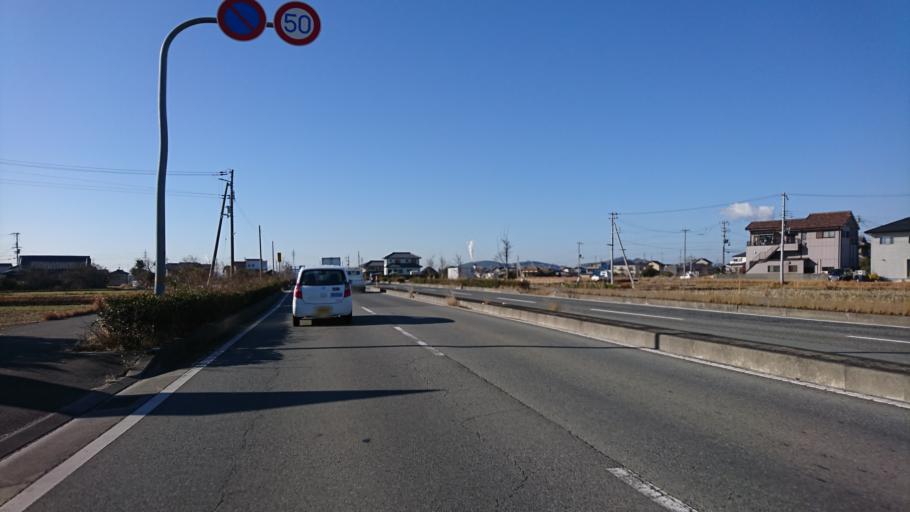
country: JP
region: Hyogo
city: Kakogawacho-honmachi
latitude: 34.7971
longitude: 134.8275
